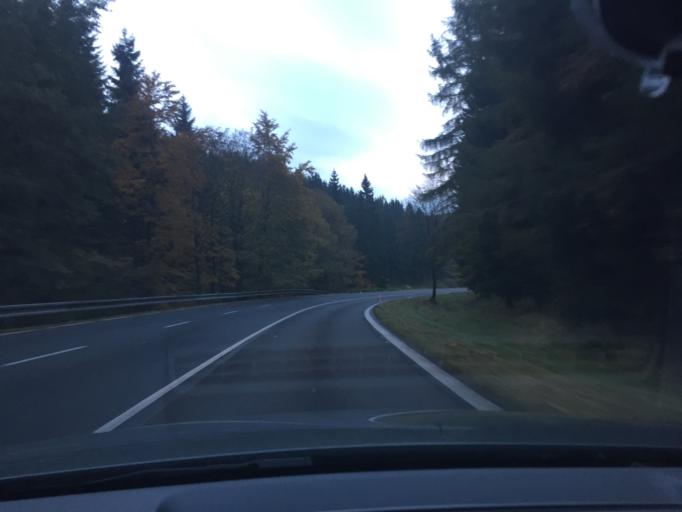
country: CZ
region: Ustecky
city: Dubi
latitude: 50.7120
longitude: 13.7759
